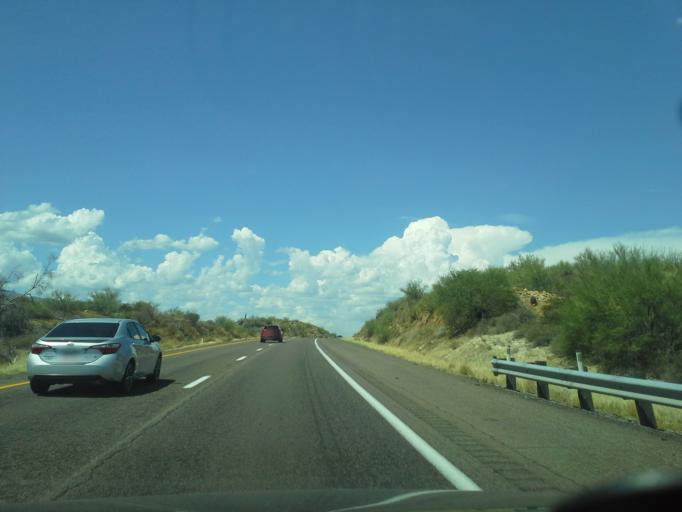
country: US
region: Arizona
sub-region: Yavapai County
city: Black Canyon City
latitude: 34.0237
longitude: -112.1447
